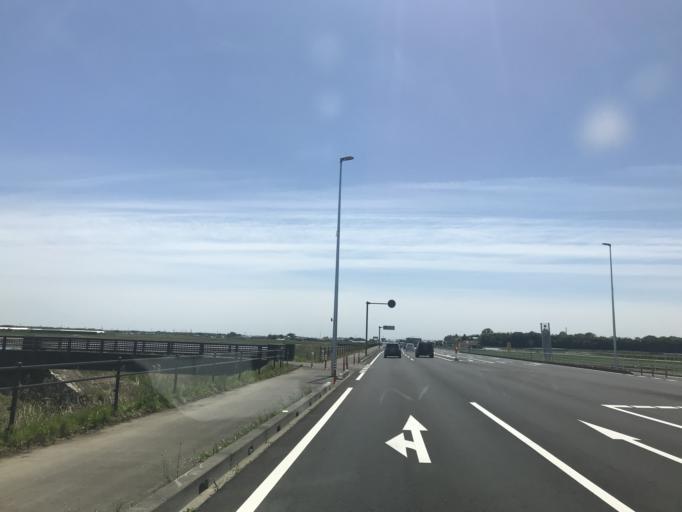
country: JP
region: Ibaraki
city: Shimodate
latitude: 36.2350
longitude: 139.9848
